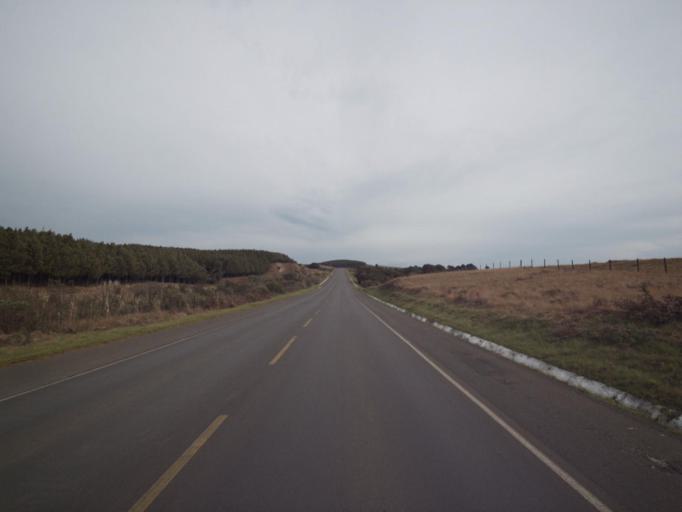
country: BR
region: Parana
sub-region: Palmas
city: Palmas
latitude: -26.7391
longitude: -51.6523
